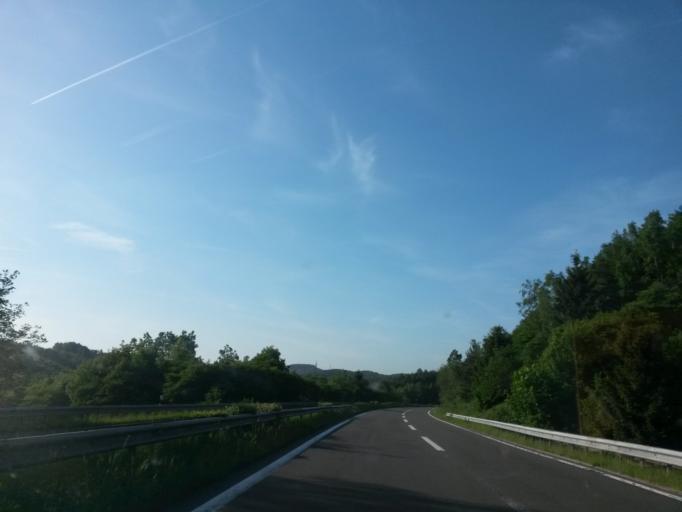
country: DE
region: North Rhine-Westphalia
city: Bergneustadt
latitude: 50.9978
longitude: 7.6375
